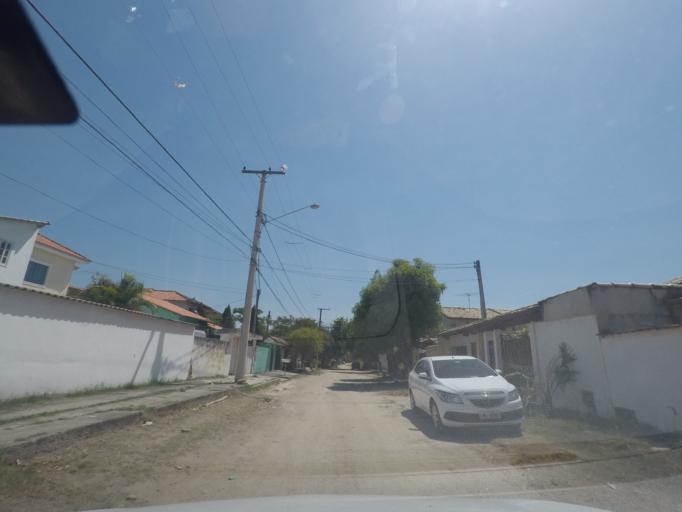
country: BR
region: Rio de Janeiro
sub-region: Niteroi
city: Niteroi
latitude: -22.9360
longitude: -43.0173
